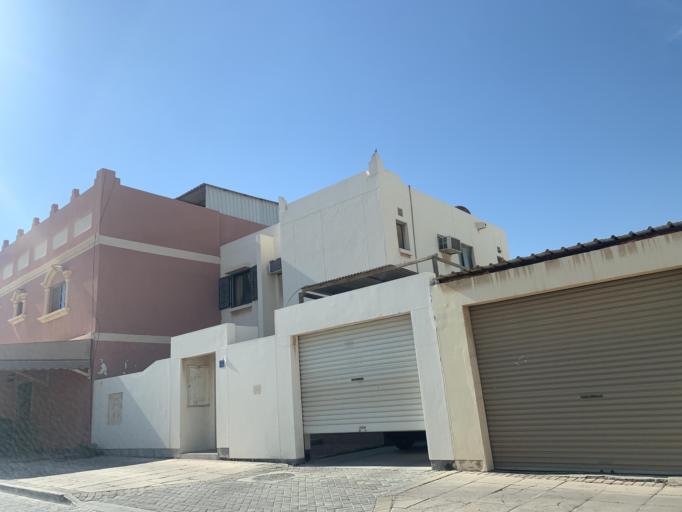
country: BH
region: Central Governorate
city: Madinat Hamad
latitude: 26.1274
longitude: 50.4969
